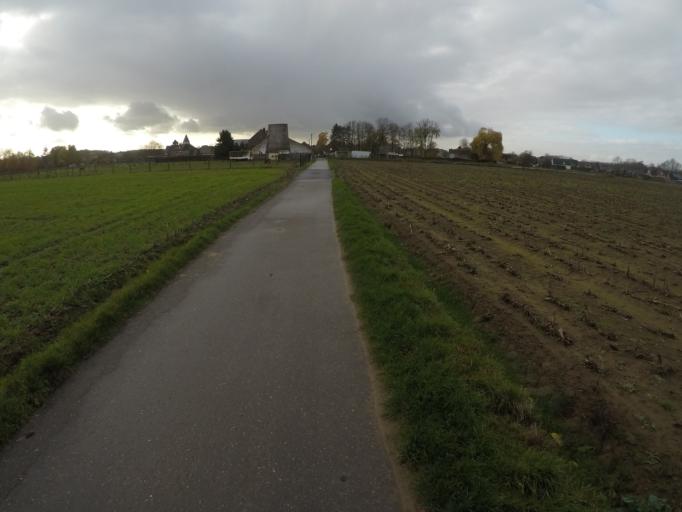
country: BE
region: Flanders
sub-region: Provincie Vlaams-Brabant
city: Opwijk
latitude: 50.9463
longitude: 4.1749
